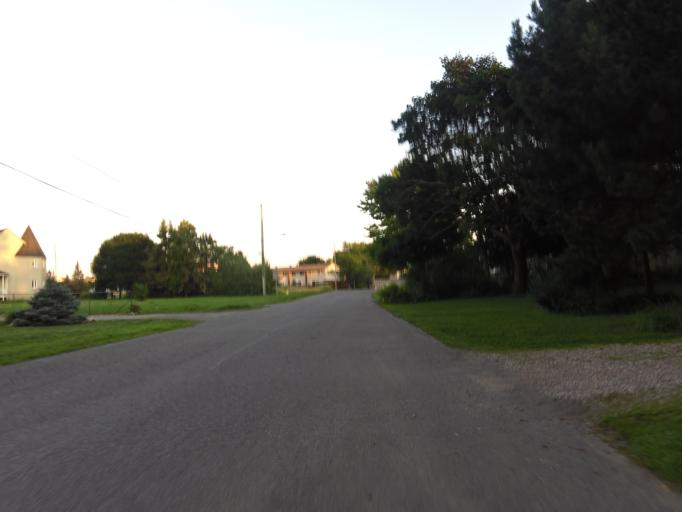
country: CA
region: Ontario
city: Bells Corners
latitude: 45.3531
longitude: -75.8358
